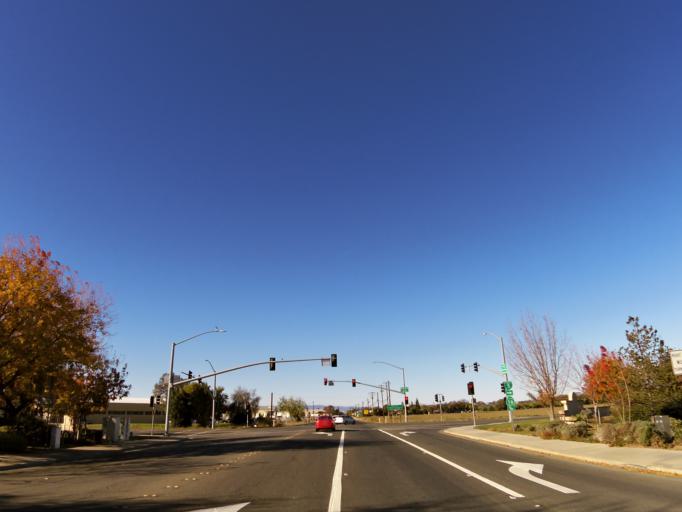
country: US
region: California
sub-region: Yolo County
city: Woodland
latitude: 38.6777
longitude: -121.8017
